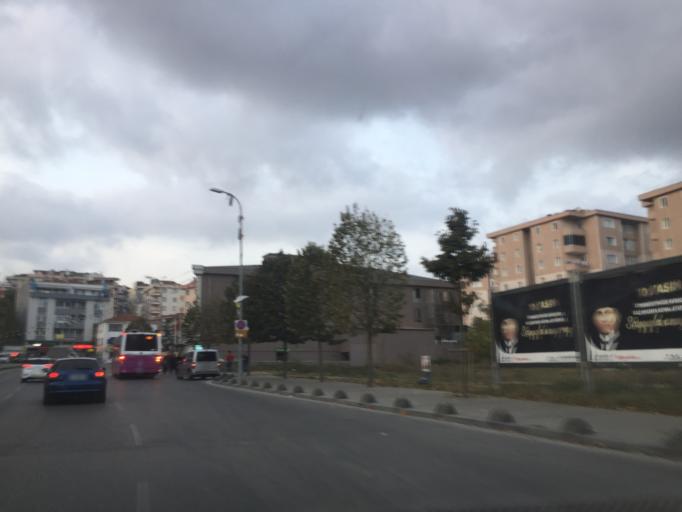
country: TR
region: Istanbul
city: Samandira
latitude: 40.9857
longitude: 29.2328
